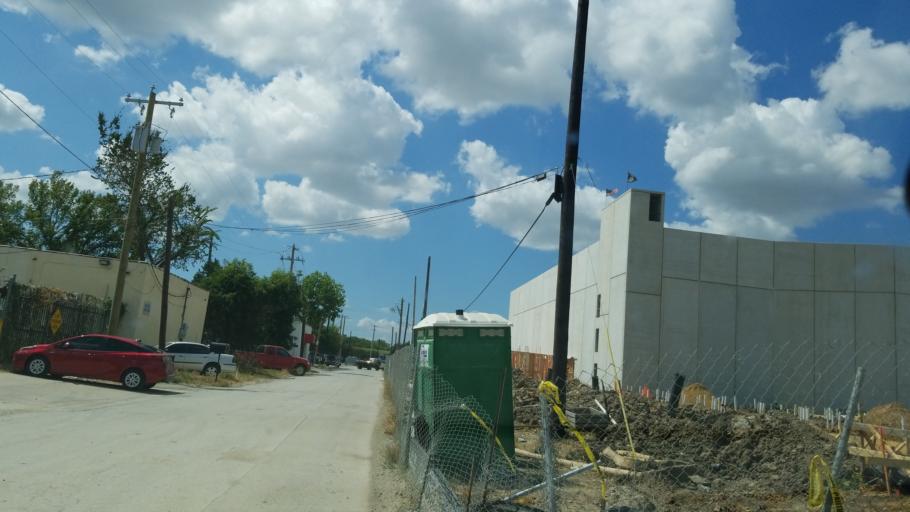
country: US
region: Texas
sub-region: Dallas County
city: Dallas
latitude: 32.7671
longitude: -96.8206
